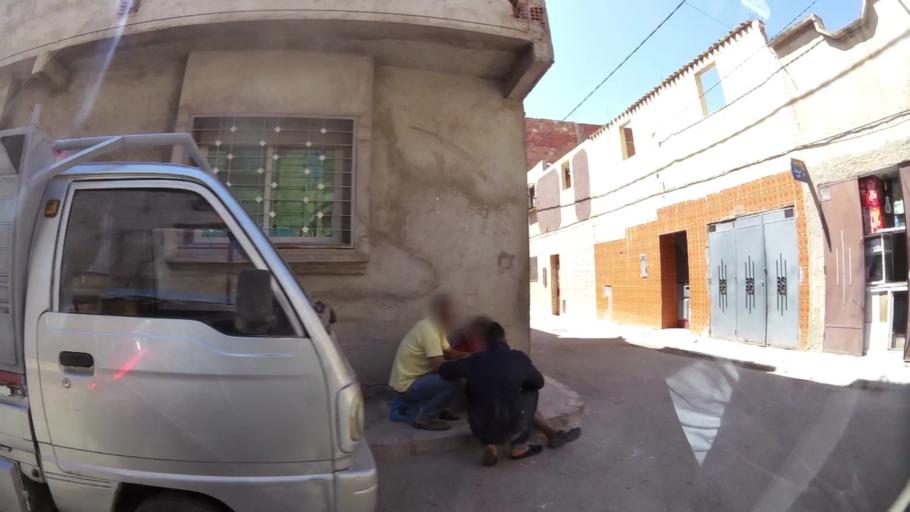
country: MA
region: Oriental
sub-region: Oujda-Angad
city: Oujda
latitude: 34.6916
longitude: -1.9412
